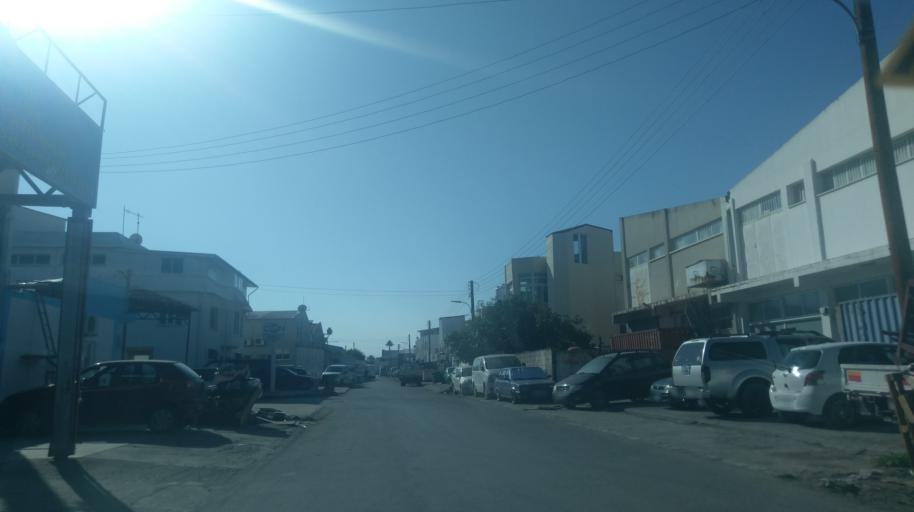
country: CY
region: Lefkosia
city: Nicosia
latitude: 35.2137
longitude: 33.3452
